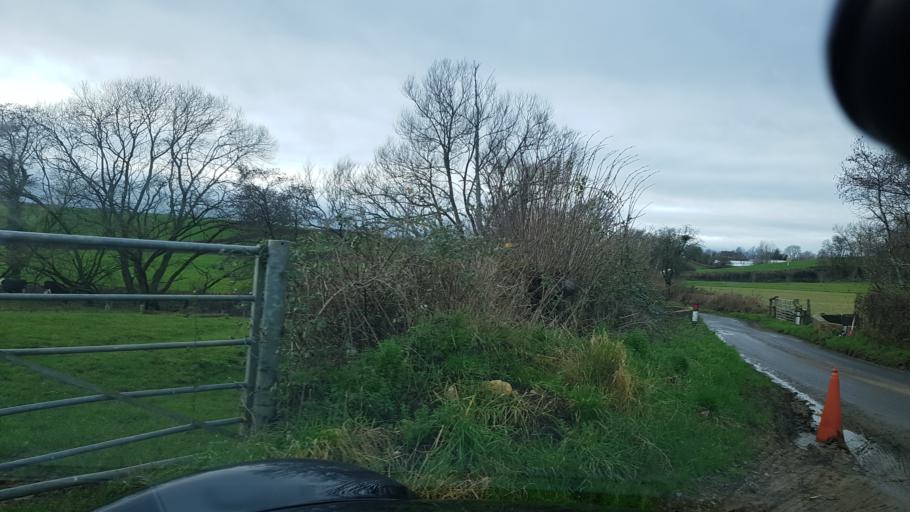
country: GB
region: England
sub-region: Somerset
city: Merriott
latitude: 50.9162
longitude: -2.7703
